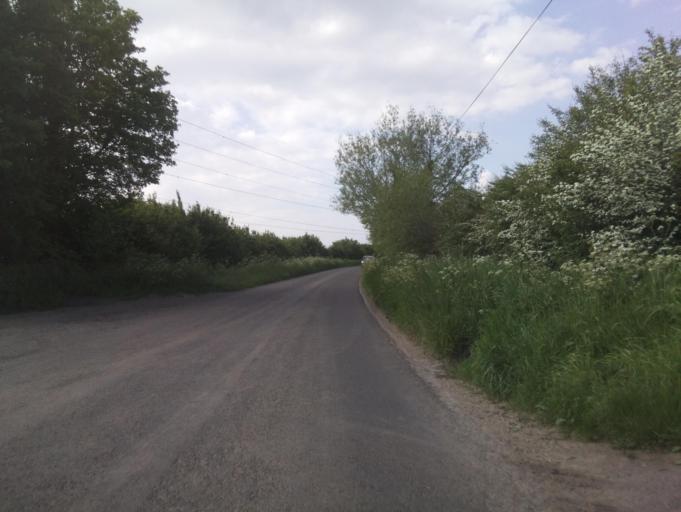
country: GB
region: England
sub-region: Wiltshire
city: Bremhill
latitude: 51.4973
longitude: -2.0738
